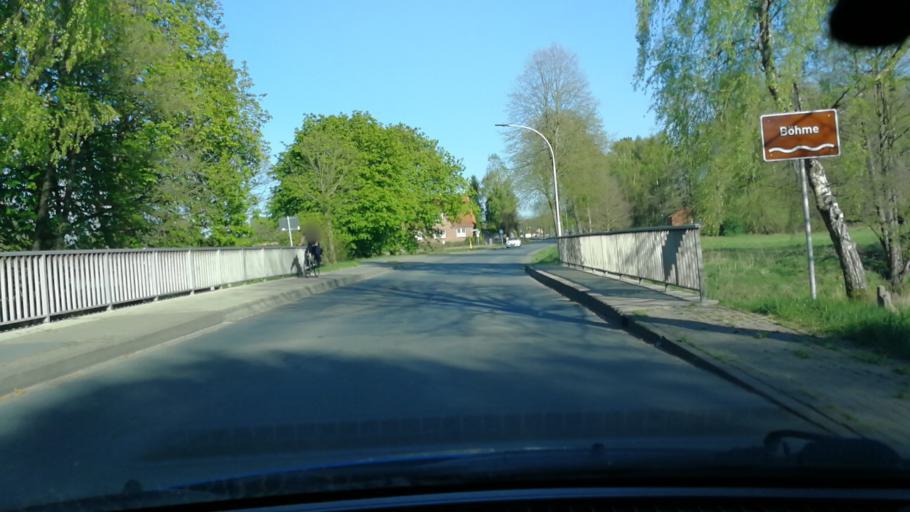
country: DE
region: Lower Saxony
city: Soltau
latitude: 52.9703
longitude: 9.8451
